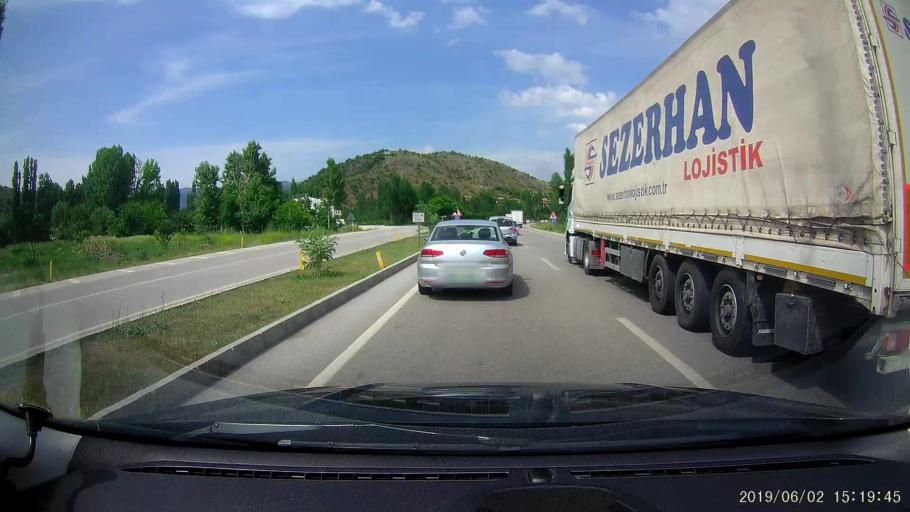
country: TR
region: Corum
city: Osmancik
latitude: 40.9743
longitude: 34.9125
